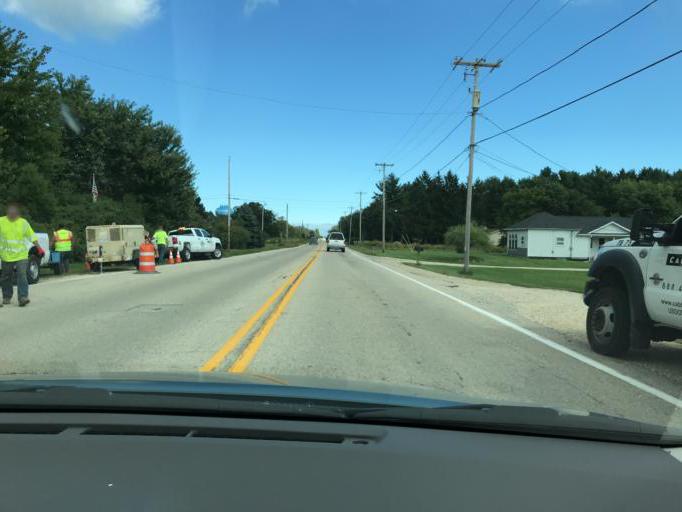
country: US
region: Wisconsin
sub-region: Kenosha County
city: Pleasant Prairie
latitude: 42.5229
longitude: -87.8839
